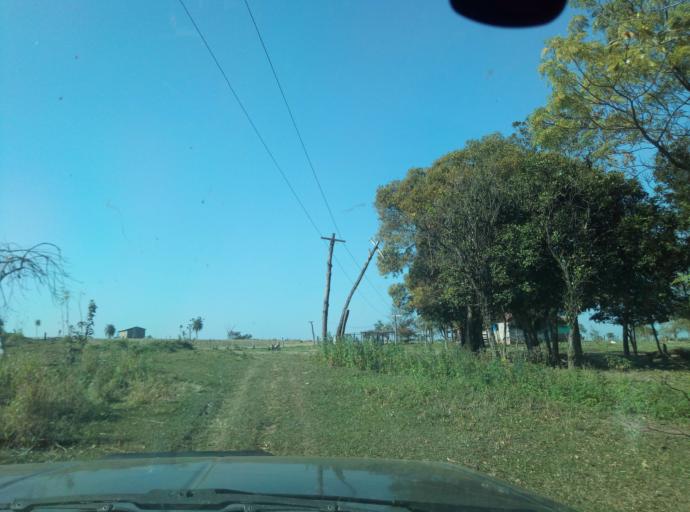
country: PY
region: Caaguazu
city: San Joaquin
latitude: -25.1764
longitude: -56.1137
